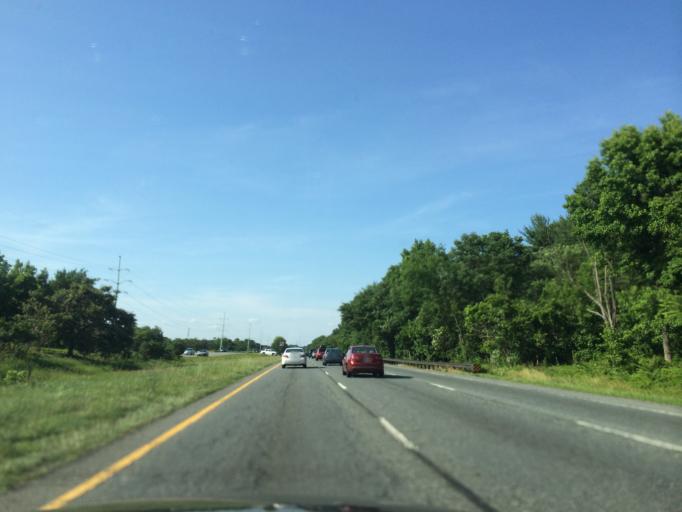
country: US
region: Maryland
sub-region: Anne Arundel County
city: Crofton
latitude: 38.9992
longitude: -76.7006
